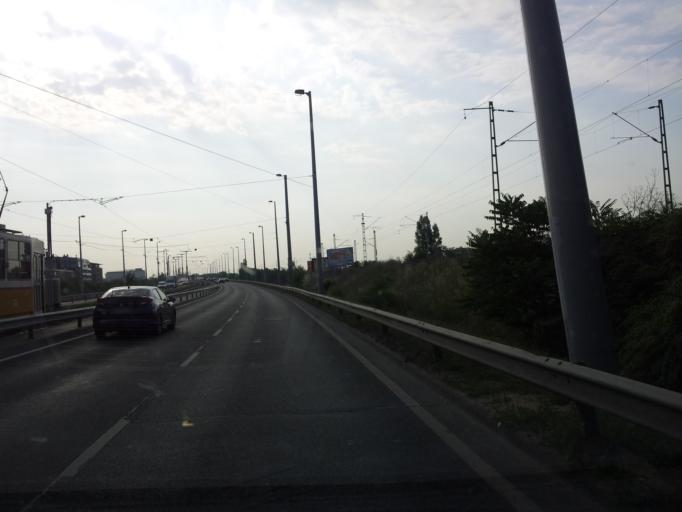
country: HU
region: Budapest
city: Budapest IX. keruelet
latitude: 47.4696
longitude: 19.0540
